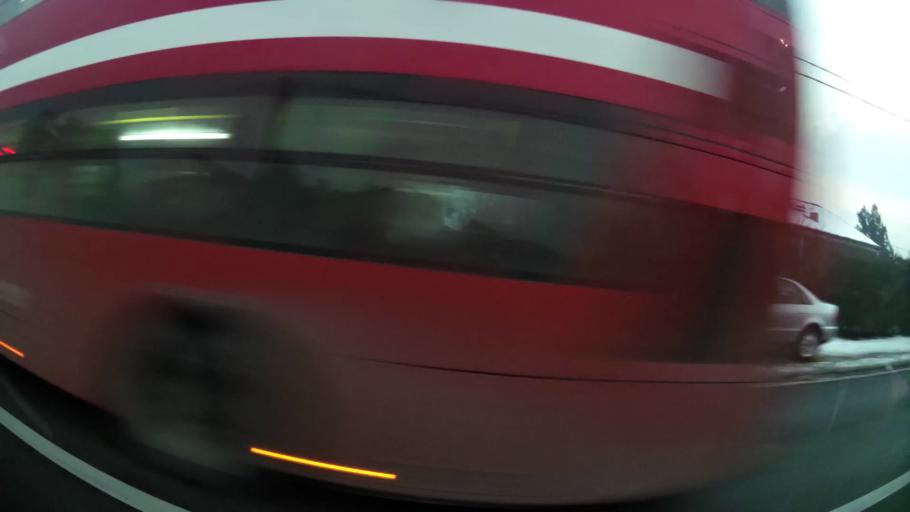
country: MK
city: Krushopek
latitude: 42.0116
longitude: 21.3780
